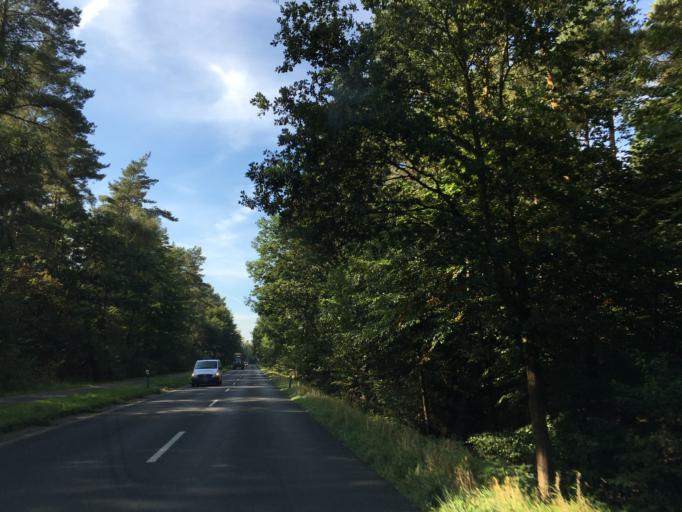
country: DE
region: Lower Saxony
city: Adendorf
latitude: 53.2909
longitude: 10.4756
